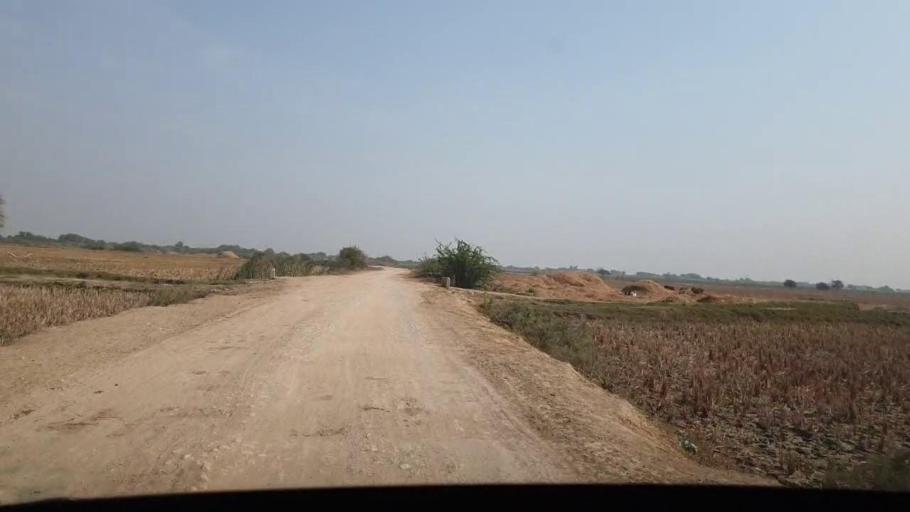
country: PK
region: Sindh
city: Chuhar Jamali
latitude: 24.2671
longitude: 67.9505
